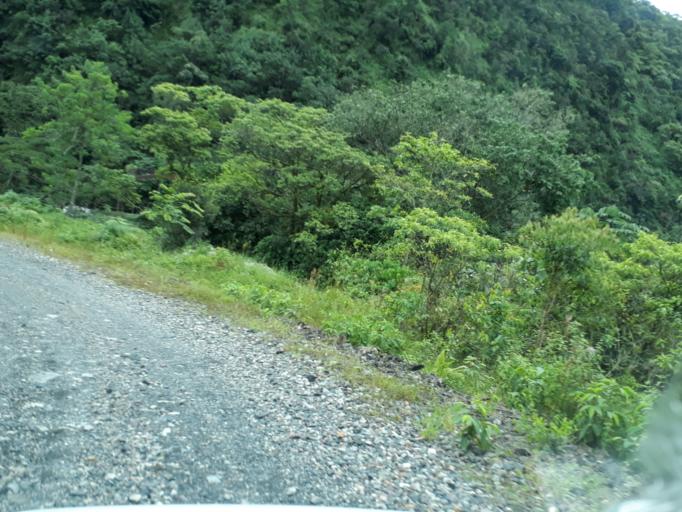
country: CO
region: Cundinamarca
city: Gachala
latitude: 4.7198
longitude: -73.3594
